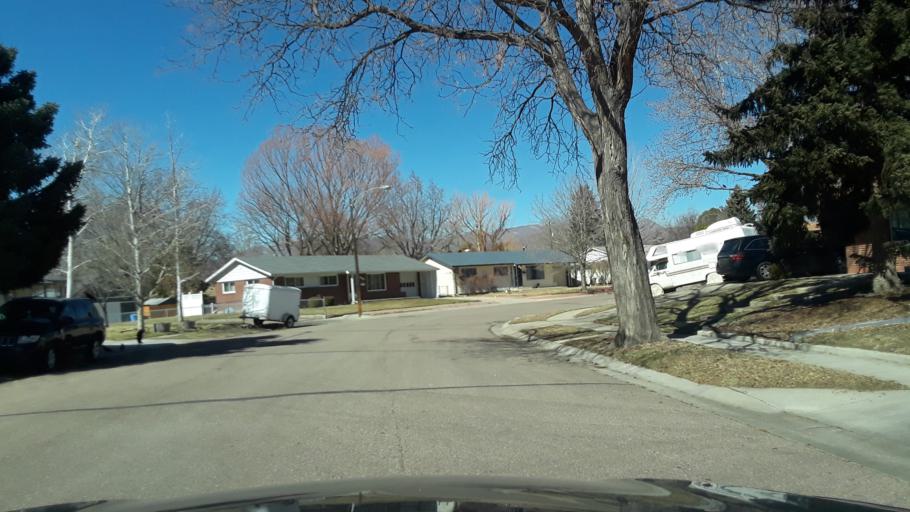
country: US
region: Colorado
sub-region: El Paso County
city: Colorado Springs
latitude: 38.8709
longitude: -104.8073
